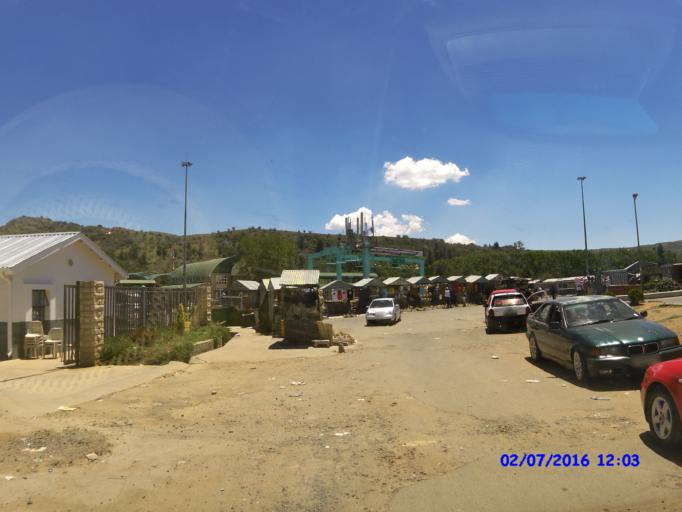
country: LS
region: Maseru
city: Maseru
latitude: -29.3001
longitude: 27.4567
